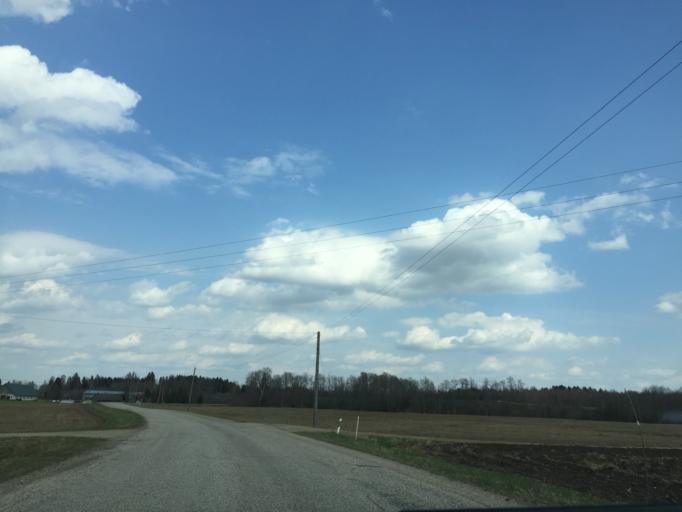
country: RU
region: Pskov
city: Pechory
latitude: 57.7172
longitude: 27.3256
